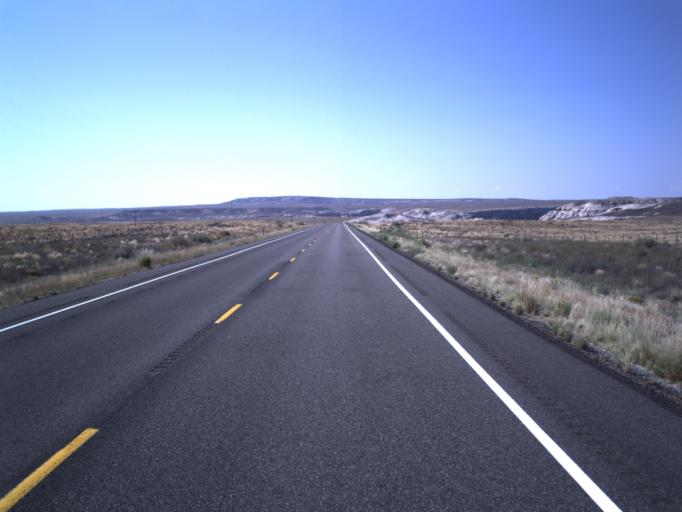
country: US
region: Utah
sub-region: San Juan County
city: Blanding
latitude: 37.3131
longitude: -109.5261
